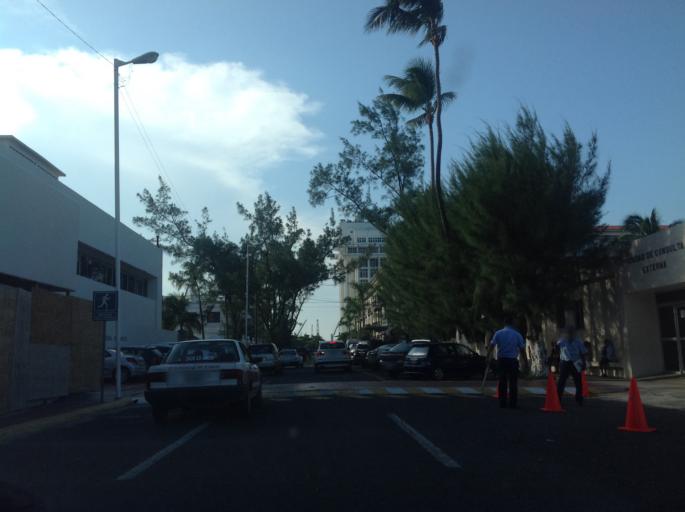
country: MX
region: Veracruz
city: Veracruz
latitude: 19.2003
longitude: -96.1315
